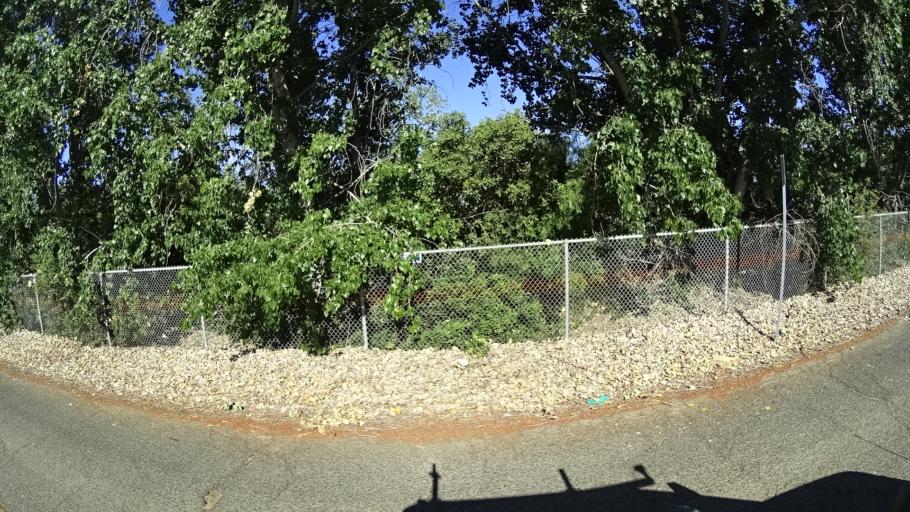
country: US
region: California
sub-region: Fresno County
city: West Park
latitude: 36.6927
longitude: -119.8270
